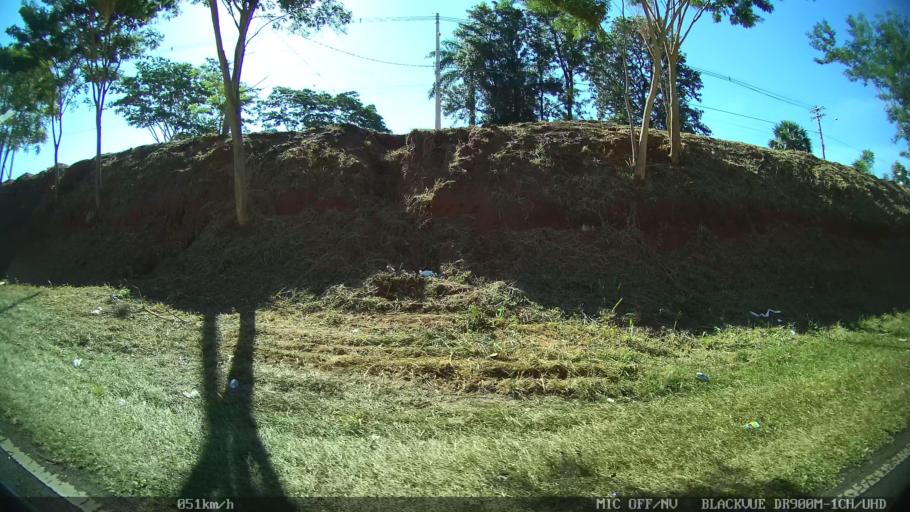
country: BR
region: Sao Paulo
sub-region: Olimpia
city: Olimpia
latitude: -20.7383
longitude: -48.8967
